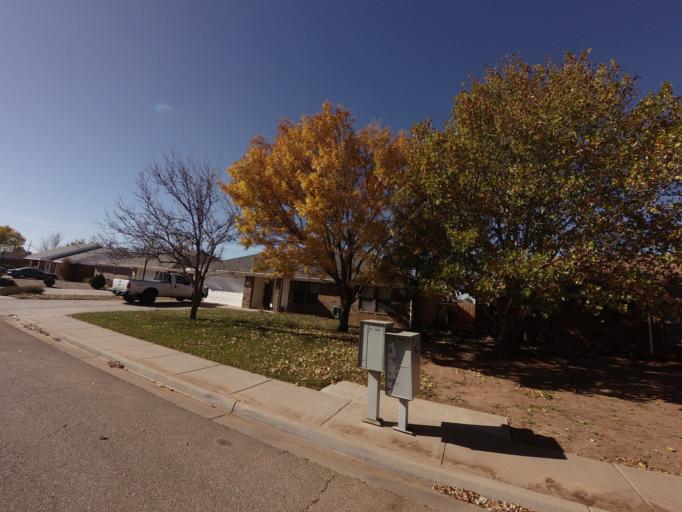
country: US
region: New Mexico
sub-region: Curry County
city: Clovis
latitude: 34.4137
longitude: -103.1694
